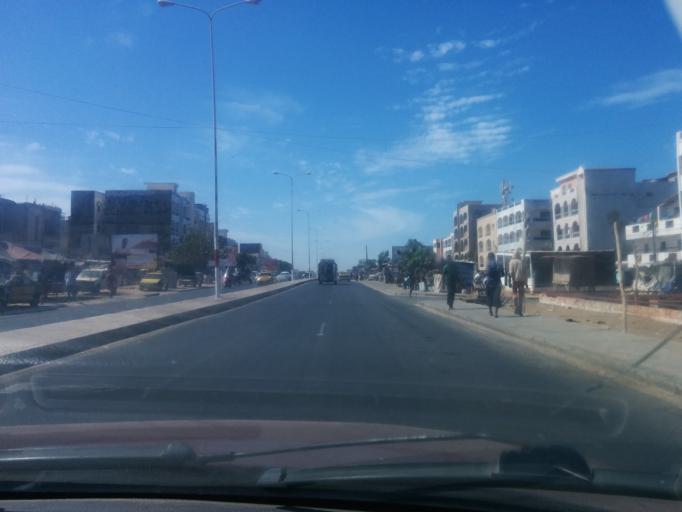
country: SN
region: Dakar
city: Pikine
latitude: 14.7767
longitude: -17.3960
